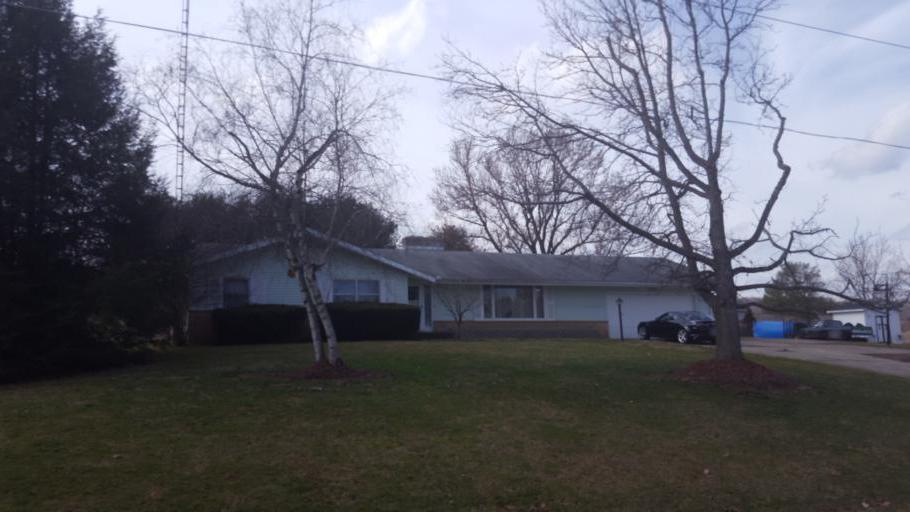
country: US
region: Ohio
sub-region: Knox County
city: Mount Vernon
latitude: 40.4226
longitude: -82.4553
